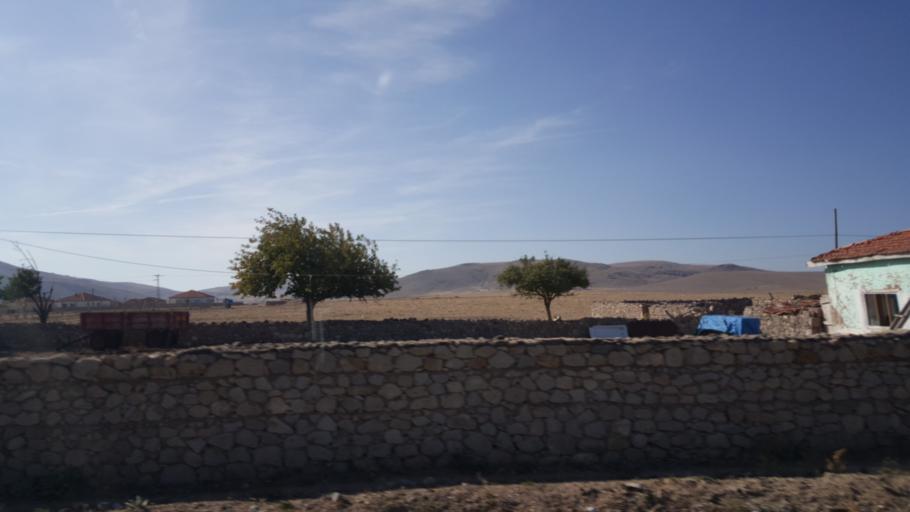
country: TR
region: Ankara
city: Altpinar
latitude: 39.2114
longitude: 32.7443
